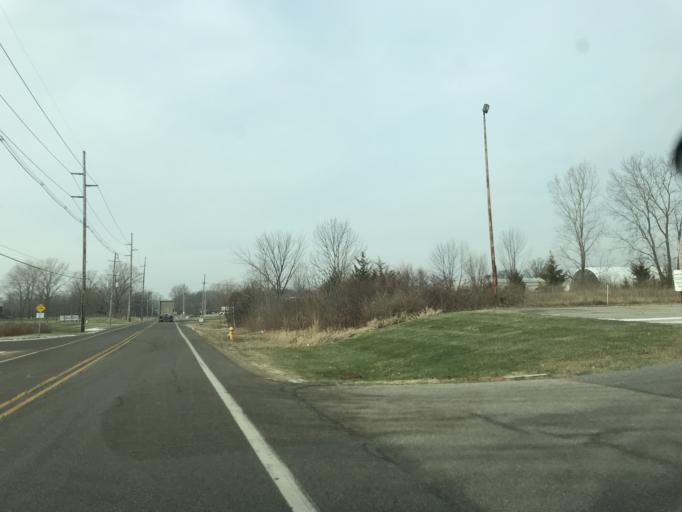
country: US
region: Michigan
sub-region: Ottawa County
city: Holland
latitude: 42.7622
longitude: -86.0809
